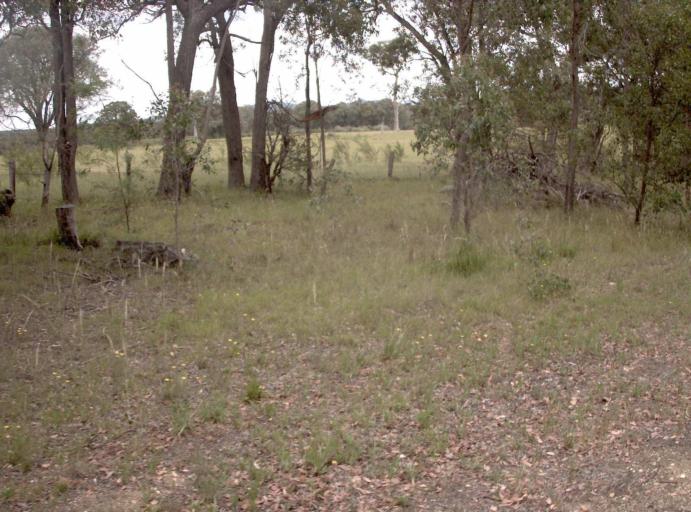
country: AU
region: Victoria
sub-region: East Gippsland
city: Bairnsdale
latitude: -37.7881
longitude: 147.3253
